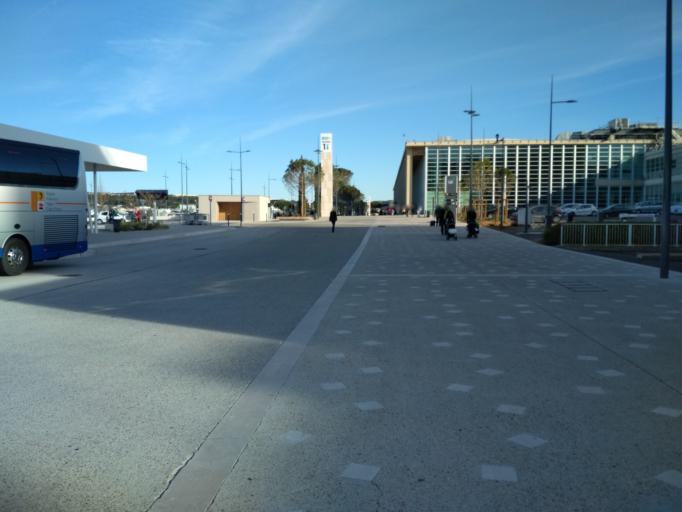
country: FR
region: Provence-Alpes-Cote d'Azur
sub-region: Departement des Bouches-du-Rhone
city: Saint-Victoret
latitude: 43.4429
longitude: 5.2204
